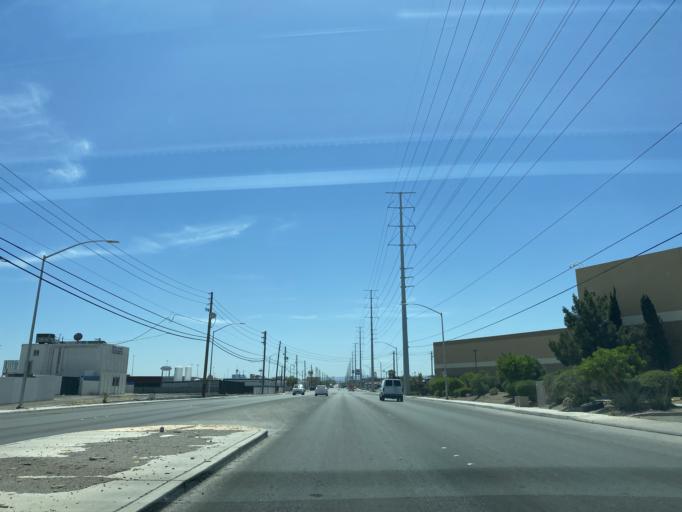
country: US
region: Nevada
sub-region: Clark County
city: North Las Vegas
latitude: 36.2265
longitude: -115.1208
